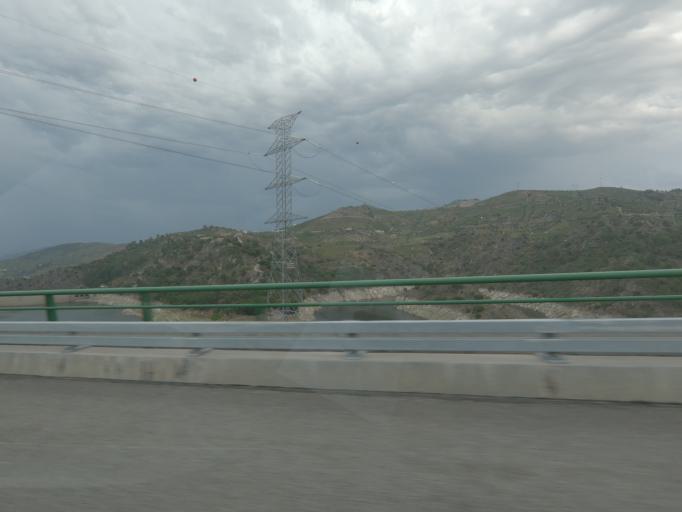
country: PT
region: Viseu
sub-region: Lamego
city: Lamego
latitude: 41.1135
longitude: -7.7779
